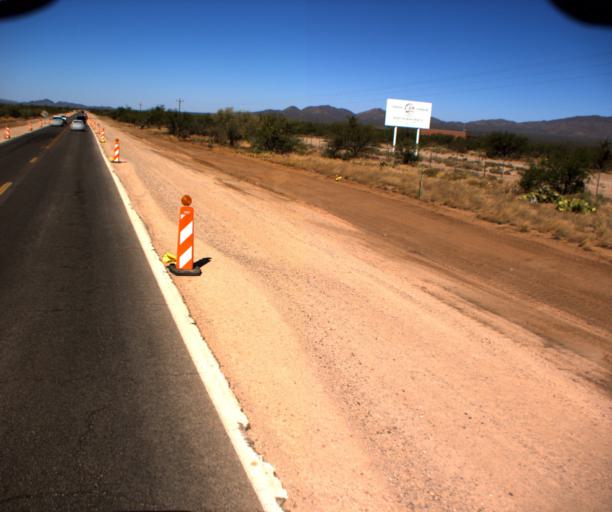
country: US
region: Arizona
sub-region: Pima County
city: Sells
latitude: 31.9898
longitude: -111.7117
